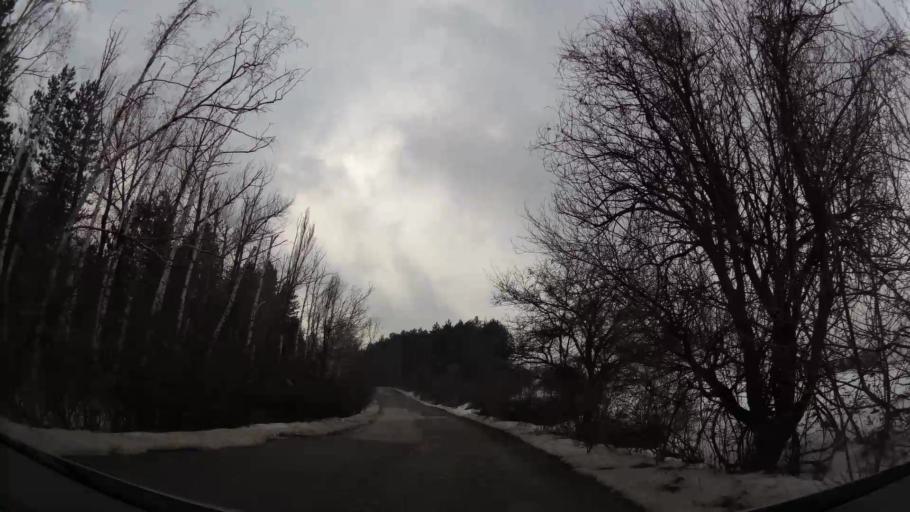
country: BG
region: Sofiya
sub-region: Obshtina Bozhurishte
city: Bozhurishte
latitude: 42.6640
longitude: 23.2127
